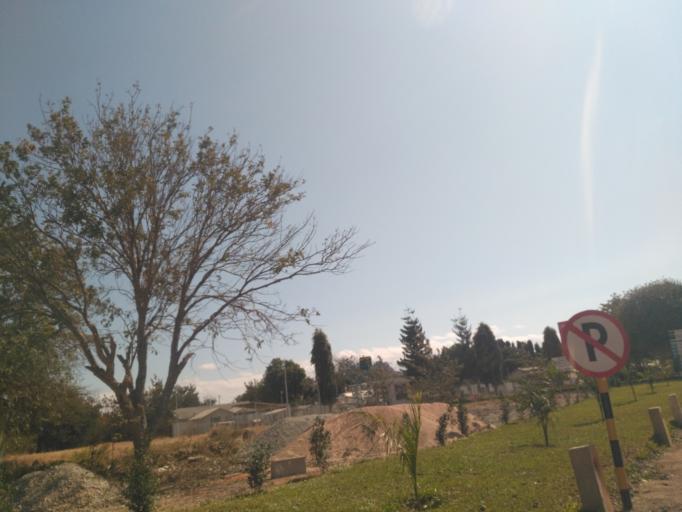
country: TZ
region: Dodoma
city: Dodoma
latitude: -6.1693
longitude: 35.7480
